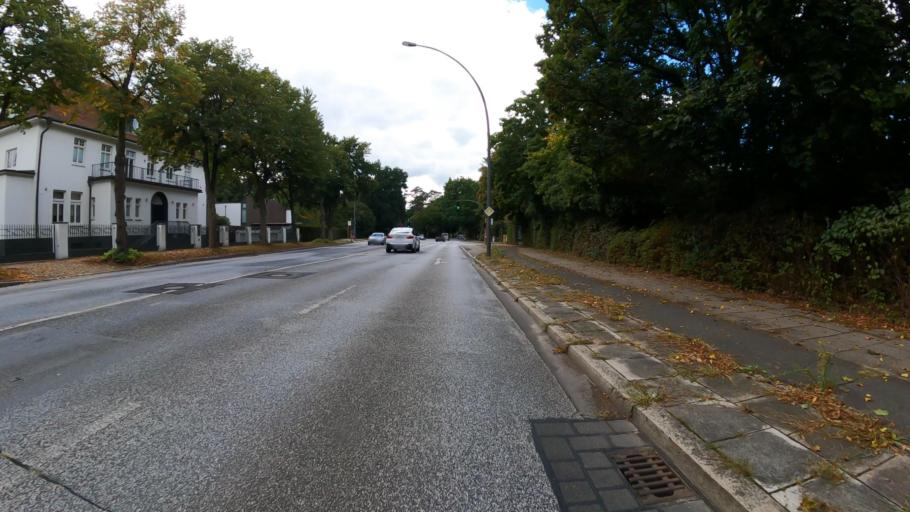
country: DE
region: Hamburg
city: Hummelsbuettel
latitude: 53.6365
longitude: 10.0447
